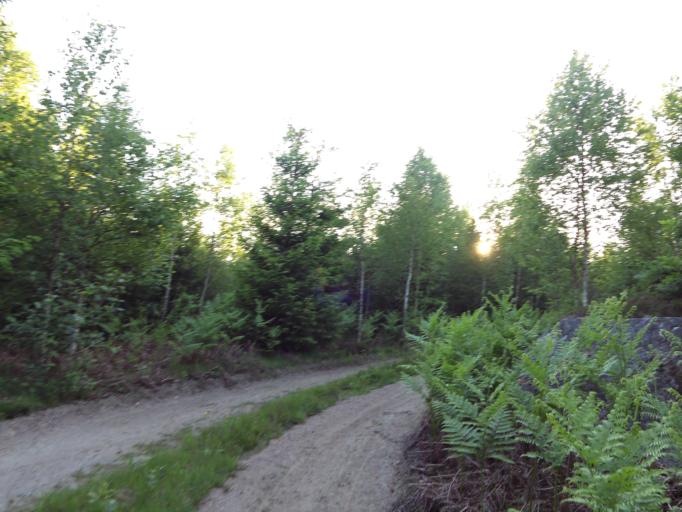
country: SE
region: Blekinge
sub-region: Olofstroms Kommun
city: Olofstroem
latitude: 56.4120
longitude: 14.5586
